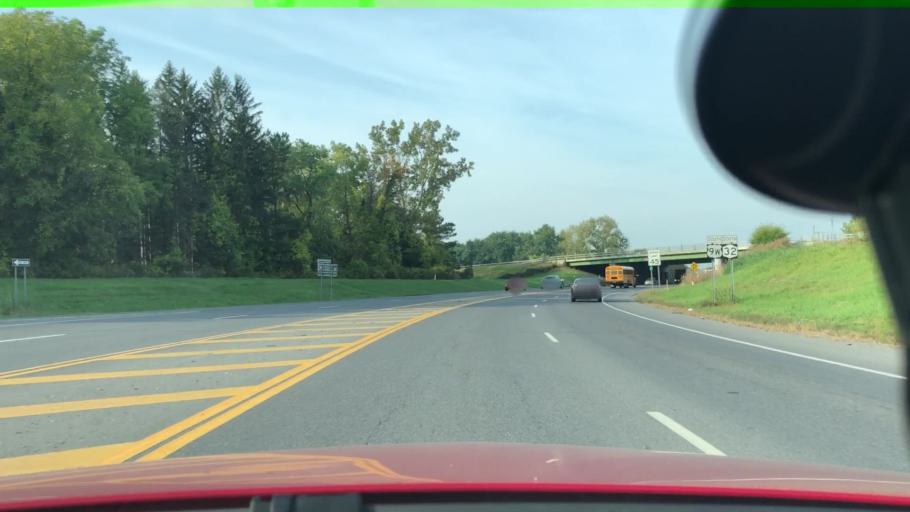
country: US
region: New York
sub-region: Albany County
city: Albany
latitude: 42.6207
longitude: -73.7788
